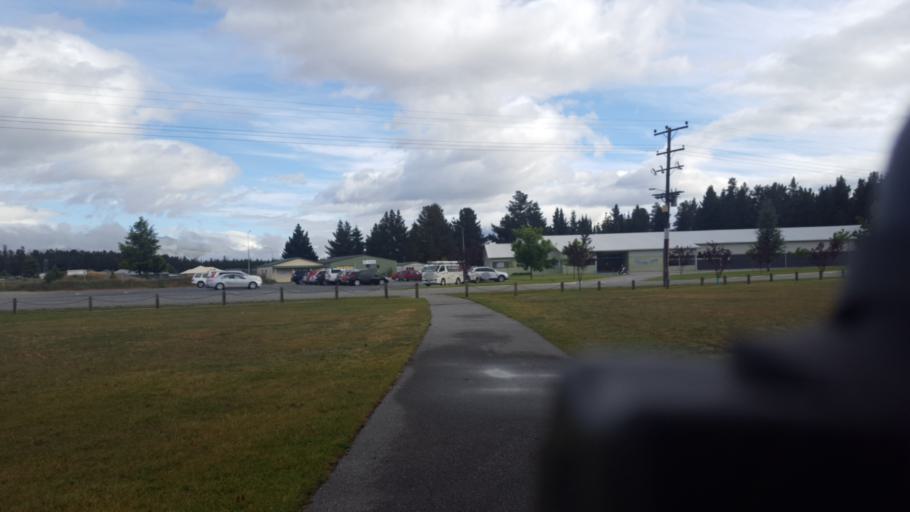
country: NZ
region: Otago
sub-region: Queenstown-Lakes District
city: Wanaka
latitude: -45.2433
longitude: 169.3819
